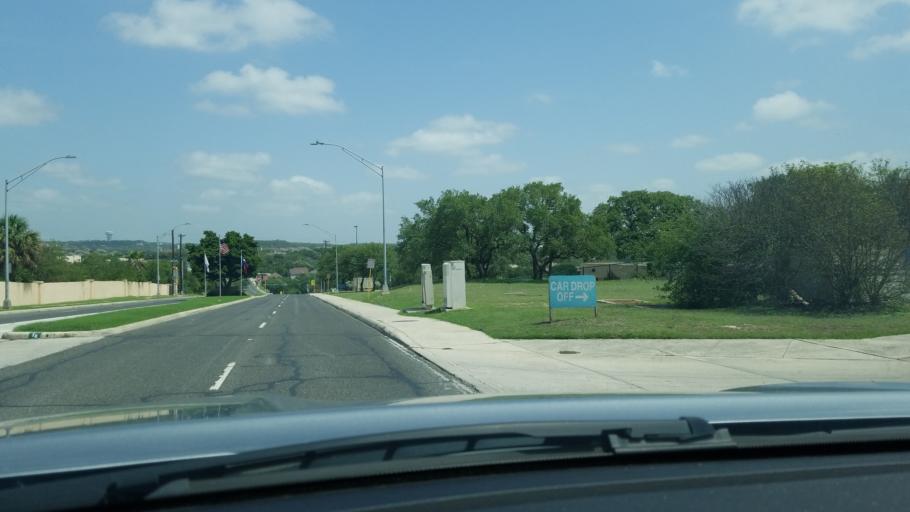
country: US
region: Texas
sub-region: Bexar County
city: Timberwood Park
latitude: 29.6547
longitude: -98.4955
